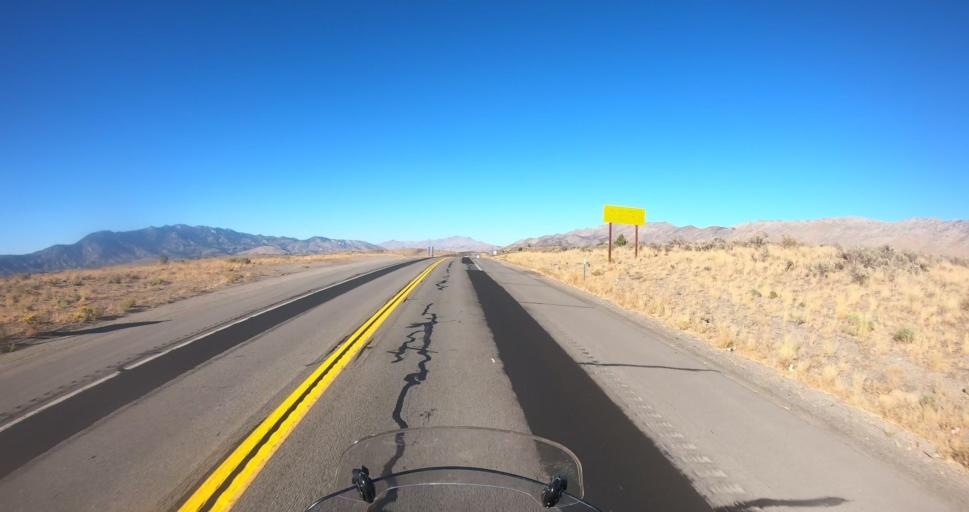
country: US
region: Nevada
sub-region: Washoe County
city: Cold Springs
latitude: 39.7912
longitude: -120.0379
